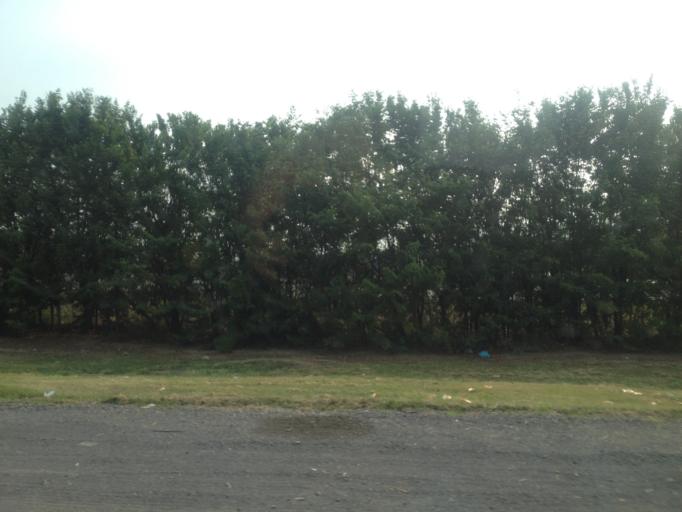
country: BR
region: Rio de Janeiro
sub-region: Porto Real
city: Porto Real
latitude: -22.4232
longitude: -44.3513
